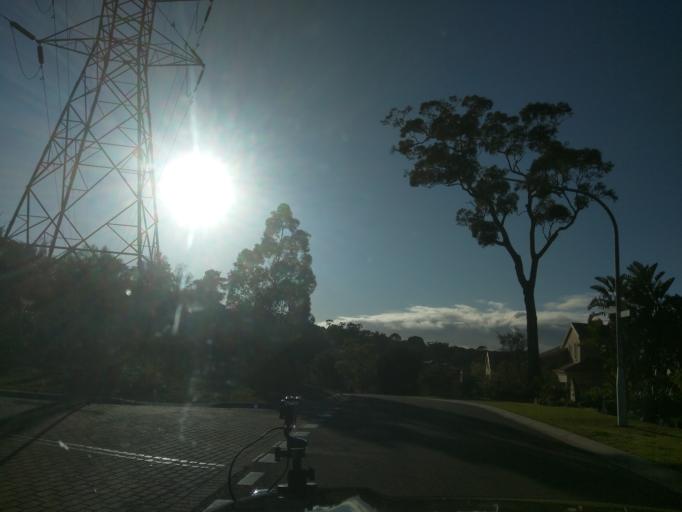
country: AU
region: New South Wales
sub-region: Sutherland Shire
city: Menai
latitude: -34.0231
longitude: 151.0230
